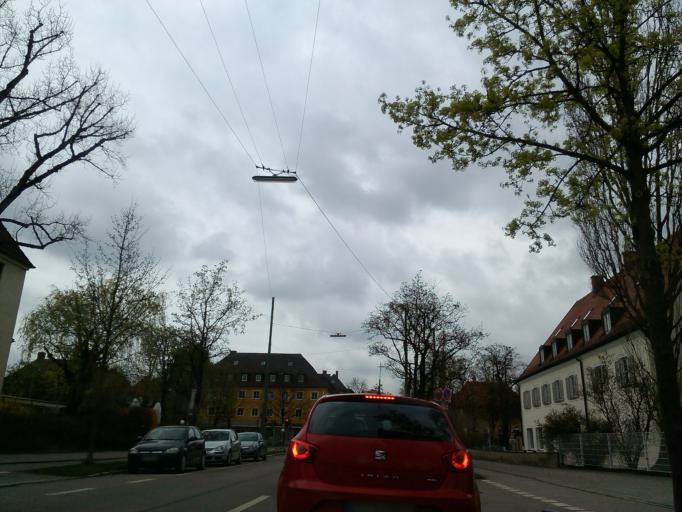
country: DE
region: Bavaria
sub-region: Upper Bavaria
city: Pasing
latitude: 48.1391
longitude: 11.4959
